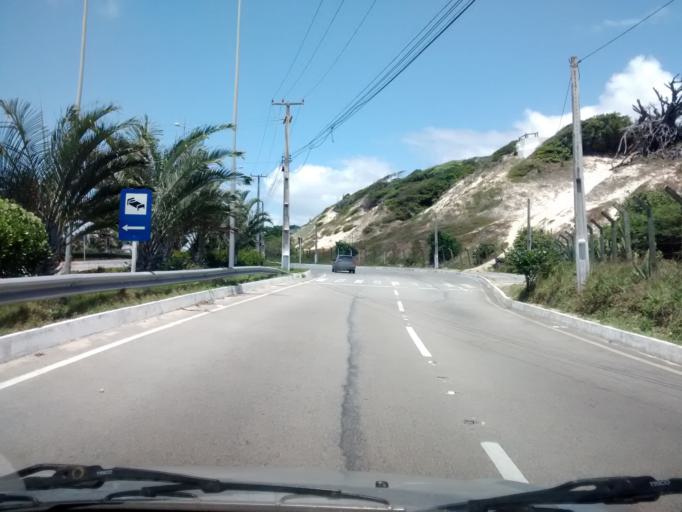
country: BR
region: Rio Grande do Norte
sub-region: Natal
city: Natal
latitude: -5.8264
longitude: -35.1833
